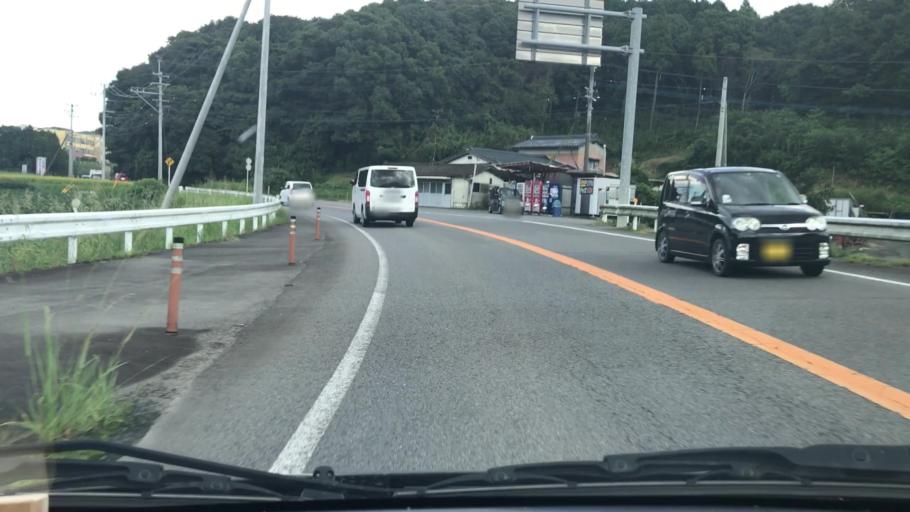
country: JP
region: Saga Prefecture
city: Takeocho-takeo
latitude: 33.2259
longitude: 130.0265
